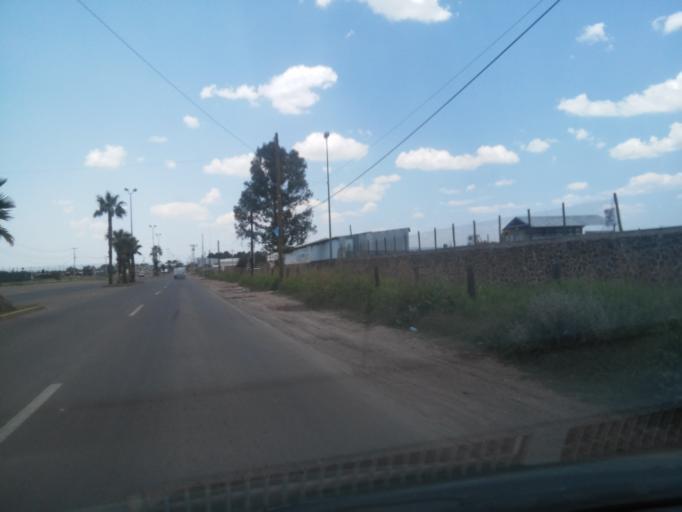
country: MX
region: Durango
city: Victoria de Durango
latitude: 24.0696
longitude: -104.6143
